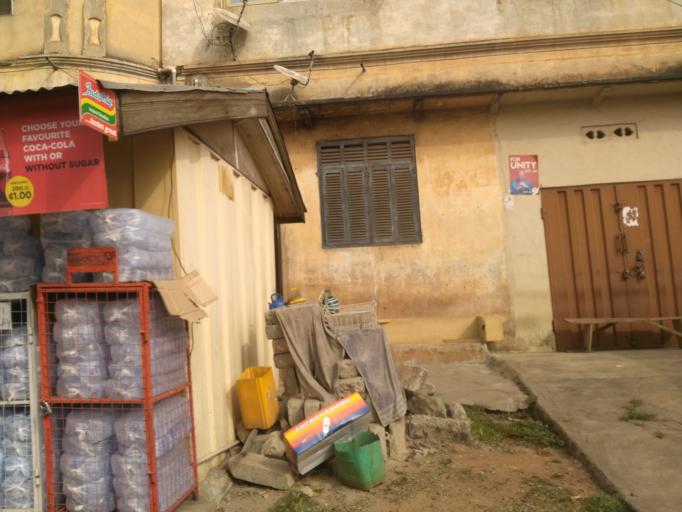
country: GH
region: Ashanti
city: Kumasi
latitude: 6.6982
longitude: -1.6099
